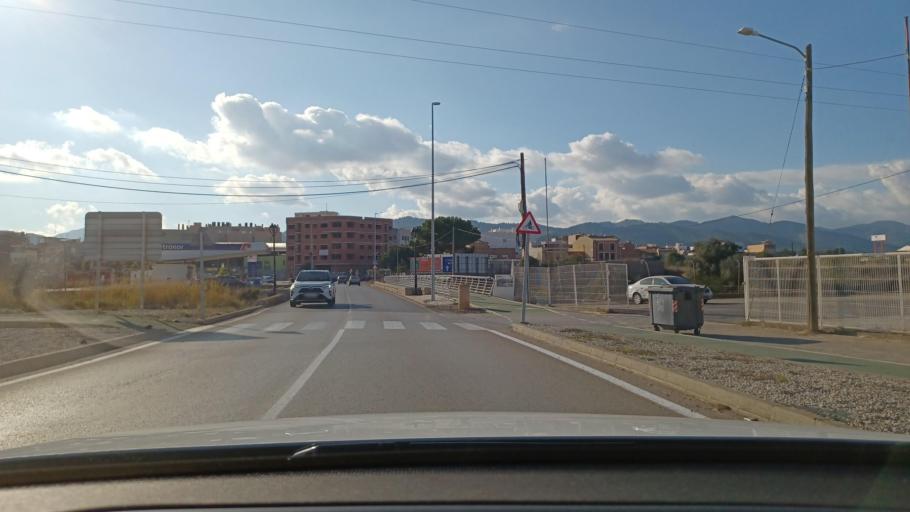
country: ES
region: Valencia
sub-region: Provincia de Castello
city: Betxi
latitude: 39.9319
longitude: -0.1951
